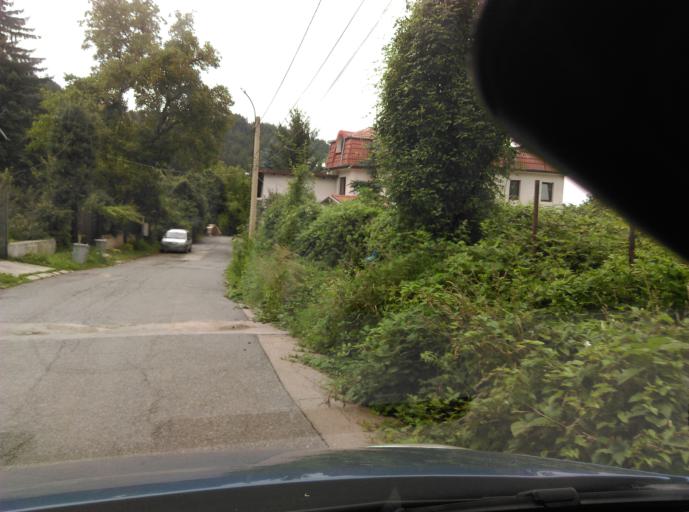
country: BG
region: Sofia-Capital
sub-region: Stolichna Obshtina
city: Sofia
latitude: 42.5984
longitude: 23.4038
